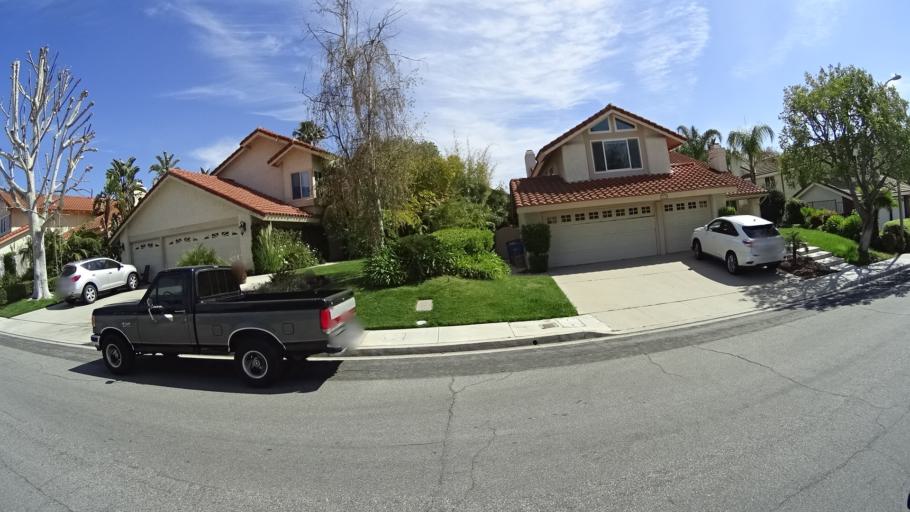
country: US
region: California
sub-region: Ventura County
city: Thousand Oaks
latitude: 34.2183
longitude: -118.8377
